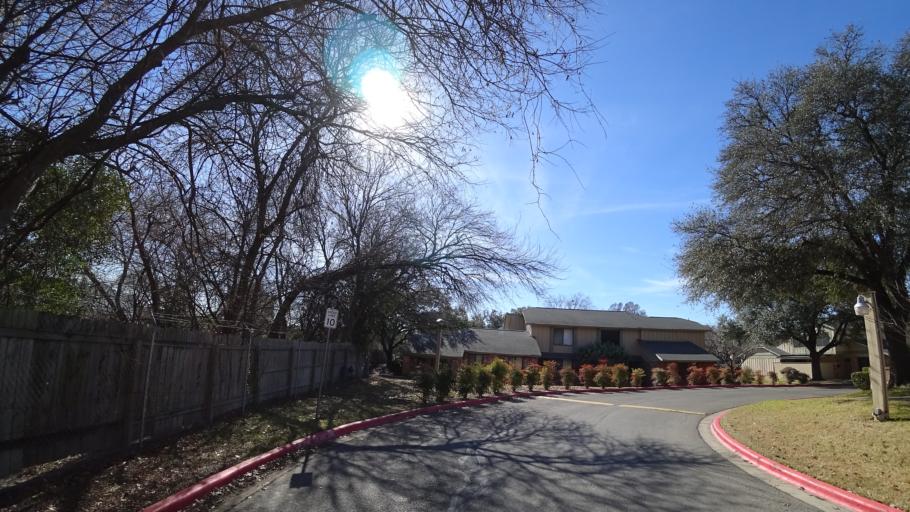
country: US
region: Texas
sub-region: Travis County
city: Wells Branch
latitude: 30.3684
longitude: -97.6971
